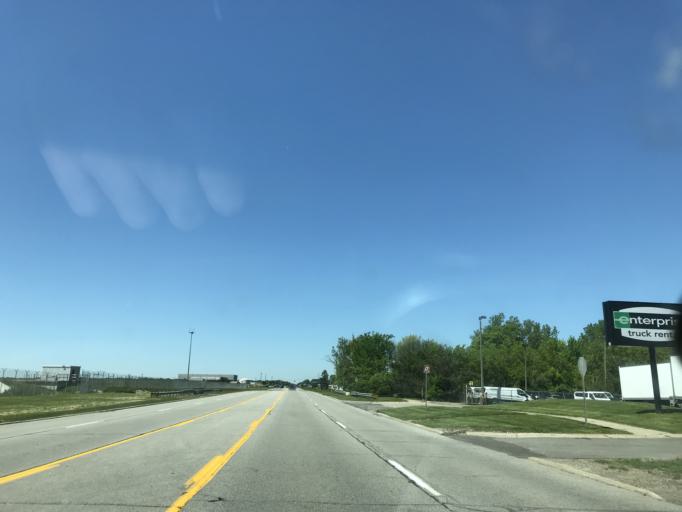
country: US
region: Michigan
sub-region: Wayne County
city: Taylor
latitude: 42.2198
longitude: -83.3271
